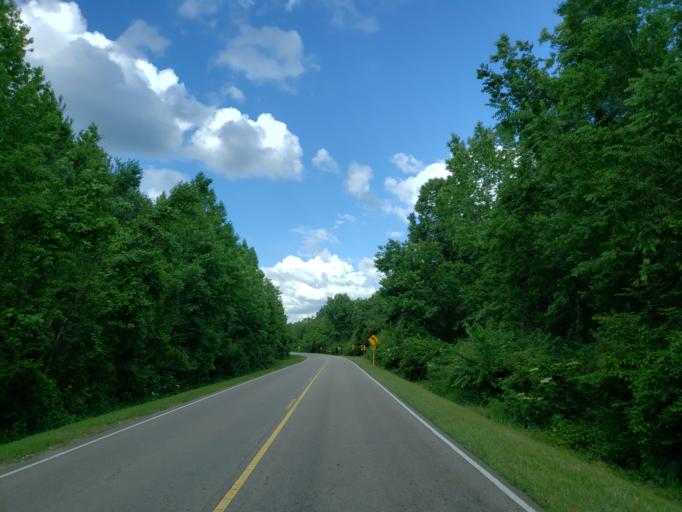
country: US
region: Mississippi
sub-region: Forrest County
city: Petal
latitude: 31.2628
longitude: -89.2188
